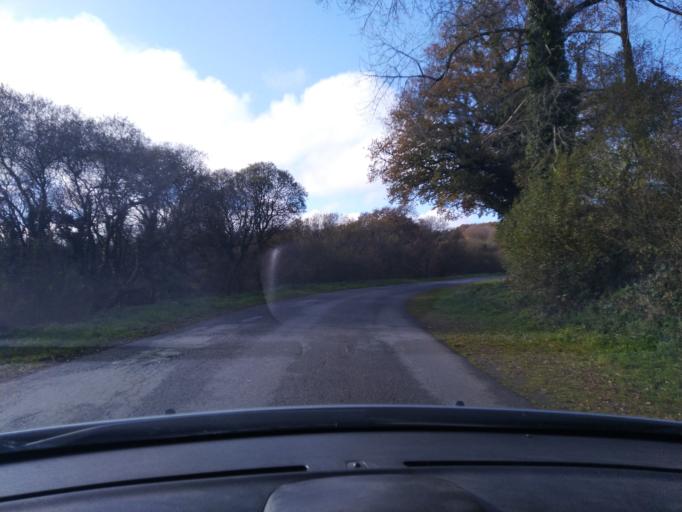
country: FR
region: Brittany
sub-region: Departement du Finistere
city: Guerlesquin
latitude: 48.5116
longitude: -3.5898
